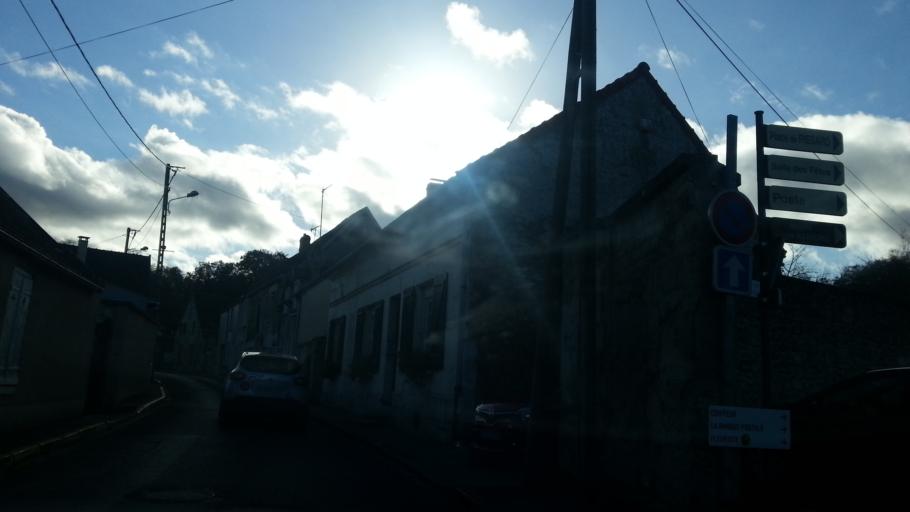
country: FR
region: Picardie
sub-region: Departement de l'Oise
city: Verneuil-en-Halatte
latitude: 49.2740
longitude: 2.5173
